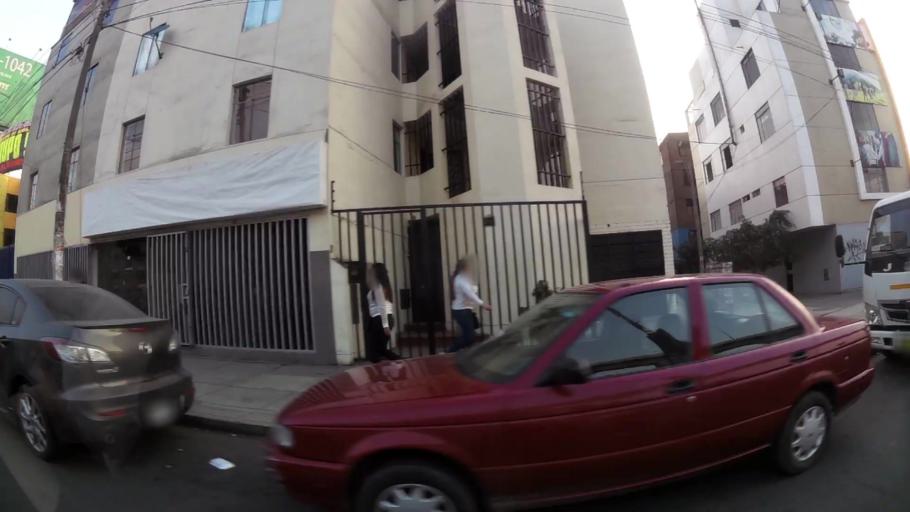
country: PE
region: Lima
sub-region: Lima
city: Independencia
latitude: -12.0049
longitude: -77.0621
